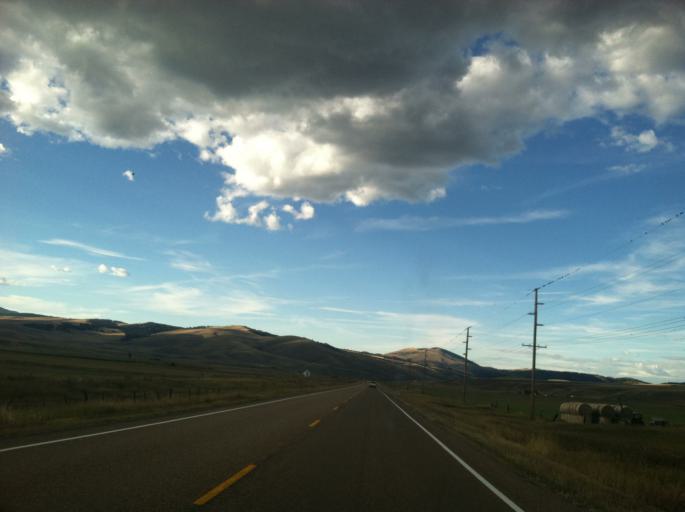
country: US
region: Montana
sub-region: Granite County
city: Philipsburg
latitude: 46.3419
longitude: -113.3120
